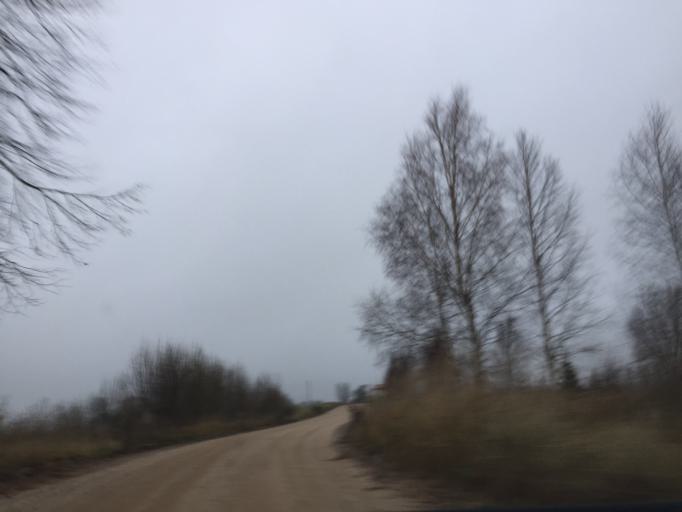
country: LV
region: Koceni
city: Koceni
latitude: 57.5488
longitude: 25.3209
